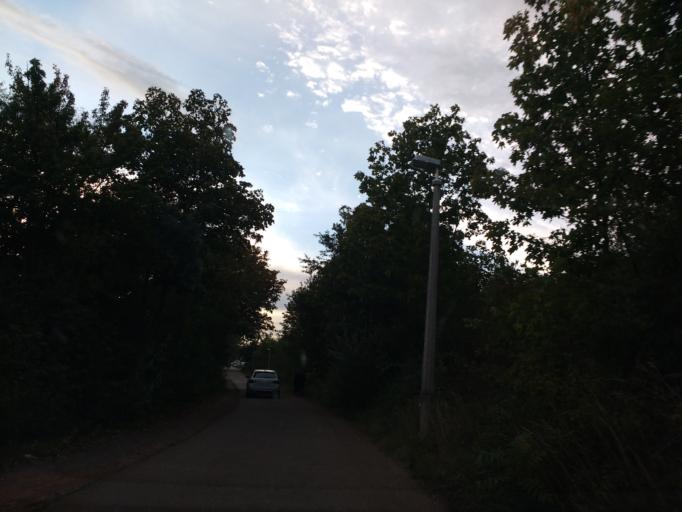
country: DE
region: Saxony-Anhalt
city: Roblingen am See
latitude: 51.4951
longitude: 11.6881
